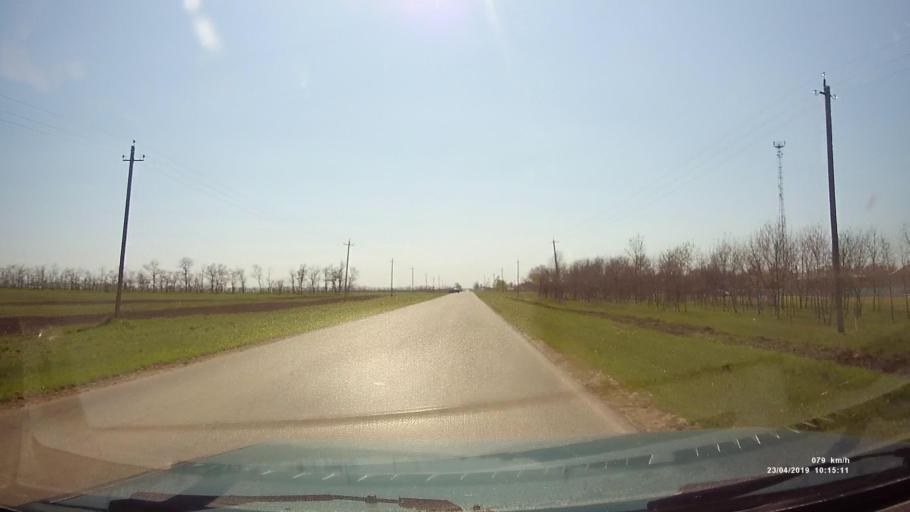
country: RU
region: Rostov
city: Sovetskoye
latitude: 46.6697
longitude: 42.3785
